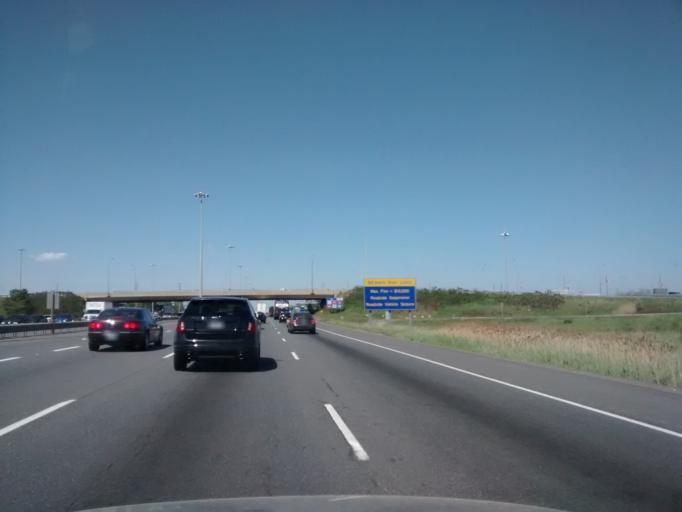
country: CA
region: Ontario
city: Burlington
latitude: 43.3649
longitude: -79.7894
